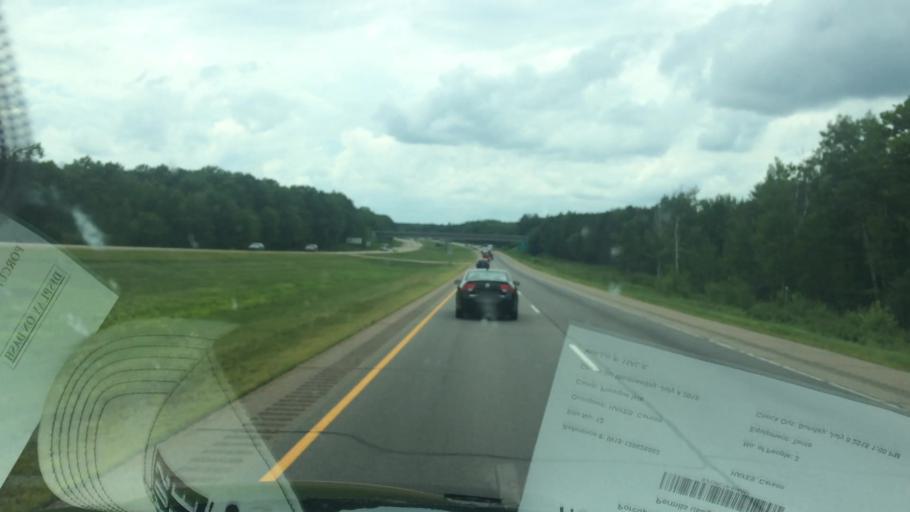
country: US
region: Wisconsin
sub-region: Marathon County
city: Mosinee
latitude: 44.7101
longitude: -89.6572
